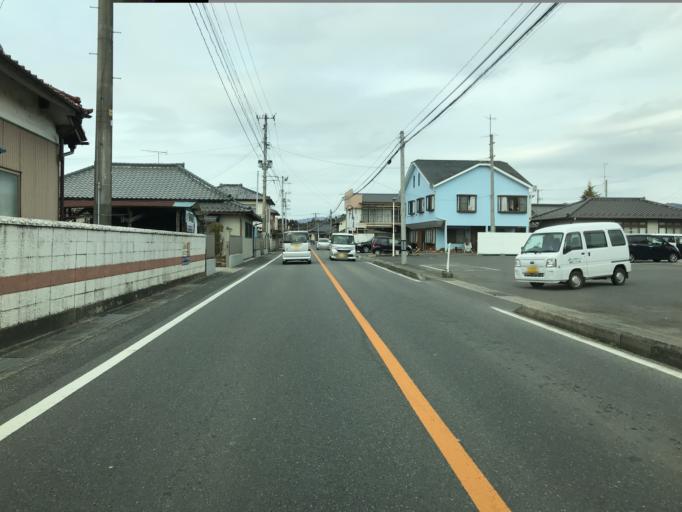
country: JP
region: Fukushima
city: Iwaki
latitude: 37.0859
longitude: 140.8771
